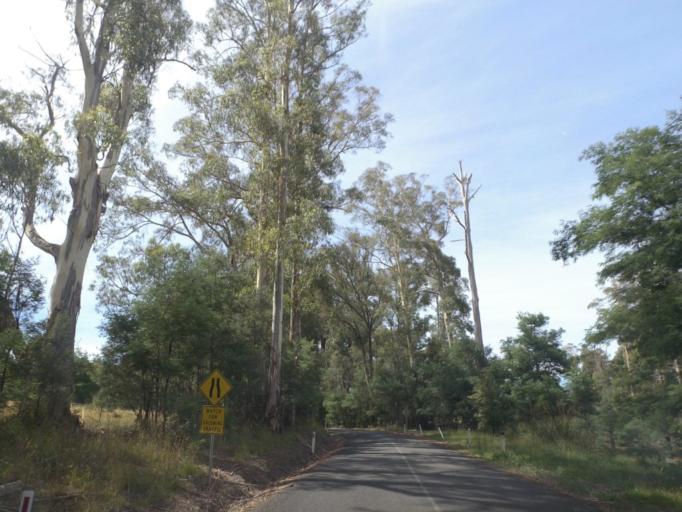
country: AU
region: Victoria
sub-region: Yarra Ranges
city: Yarra Glen
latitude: -37.5116
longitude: 145.4253
